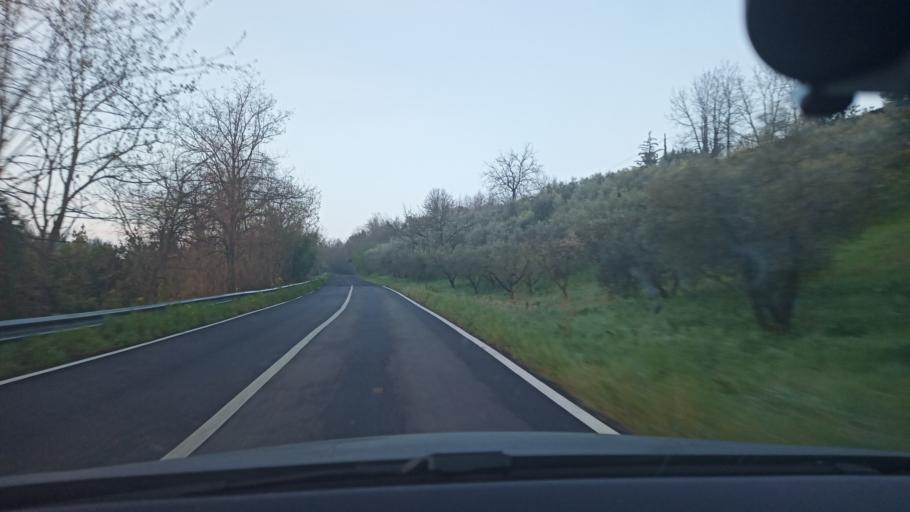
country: IT
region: Latium
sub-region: Provincia di Rieti
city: Cantalupo in Sabina
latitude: 42.3133
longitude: 12.6437
